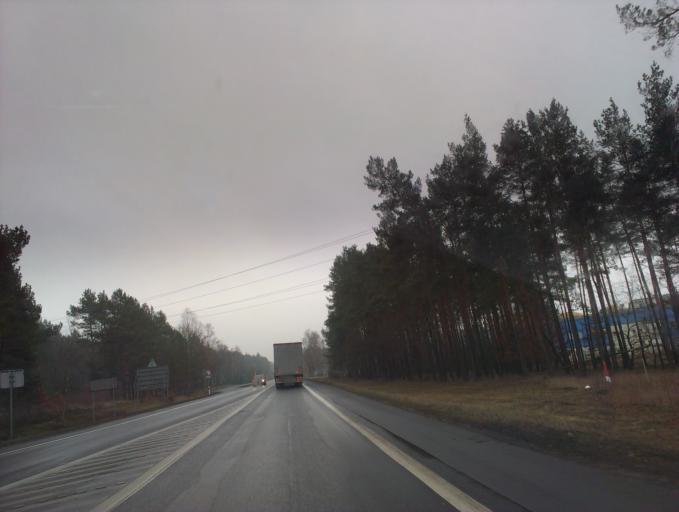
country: PL
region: Greater Poland Voivodeship
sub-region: Powiat pilski
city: Pila
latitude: 53.1710
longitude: 16.7796
